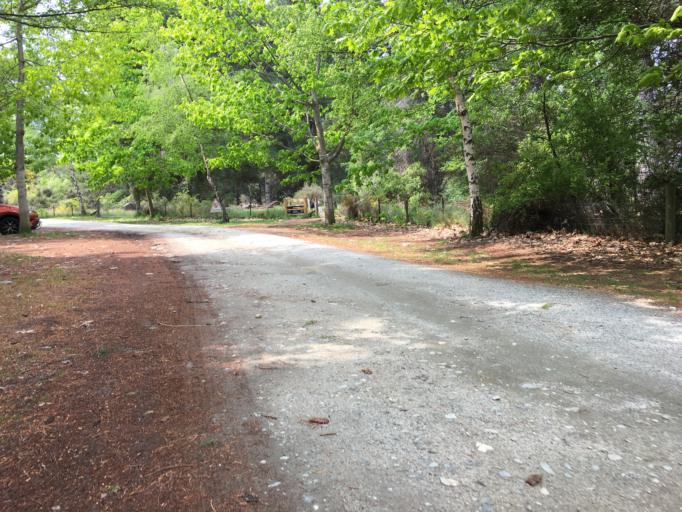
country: NZ
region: Otago
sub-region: Queenstown-Lakes District
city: Queenstown
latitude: -45.0468
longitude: 168.6899
